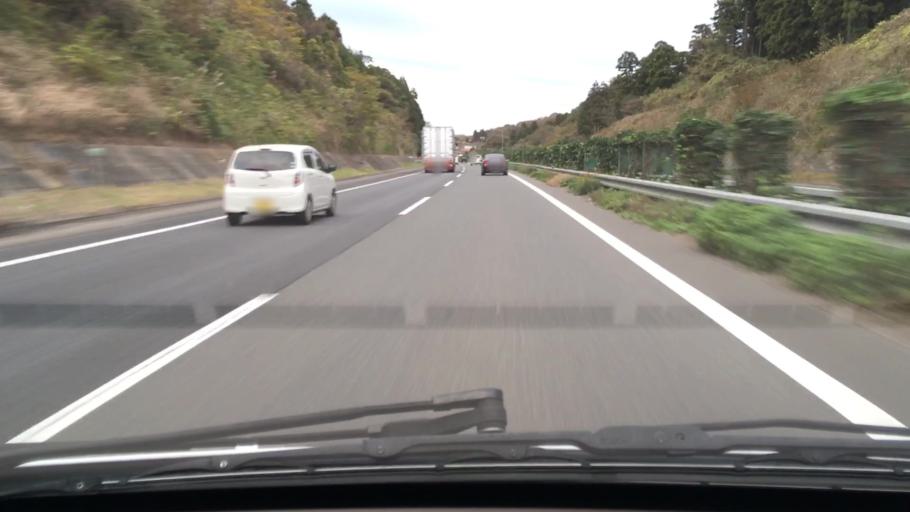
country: JP
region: Chiba
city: Ichihara
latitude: 35.4538
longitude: 140.0822
